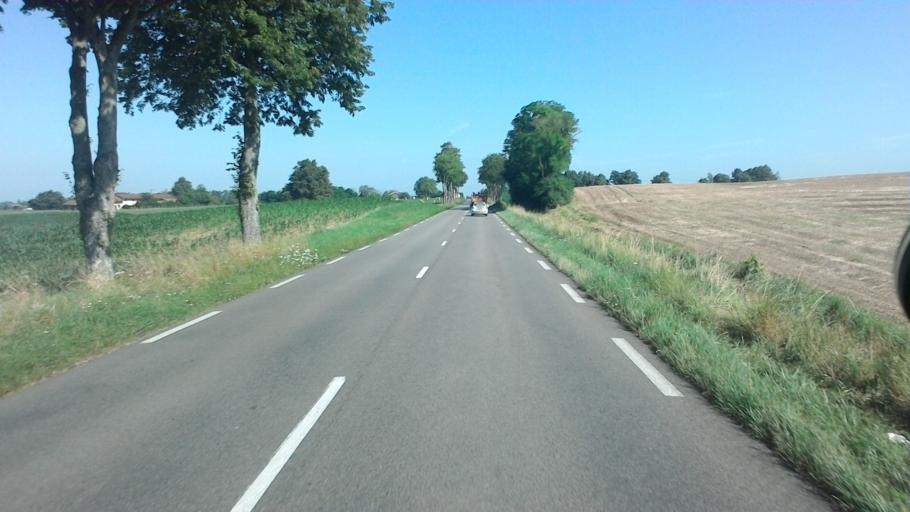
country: FR
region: Rhone-Alpes
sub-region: Departement de l'Ain
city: Saint-Trivier-de-Courtes
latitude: 46.4381
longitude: 5.0925
